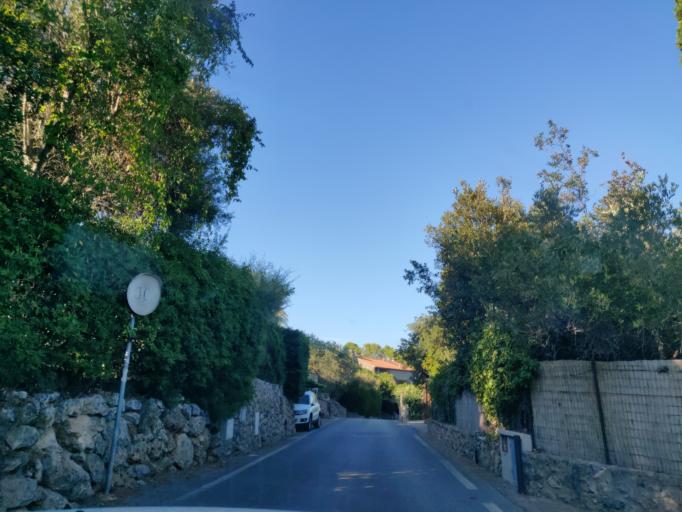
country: IT
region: Tuscany
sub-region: Provincia di Grosseto
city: Orbetello Scalo
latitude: 42.4115
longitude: 11.2925
